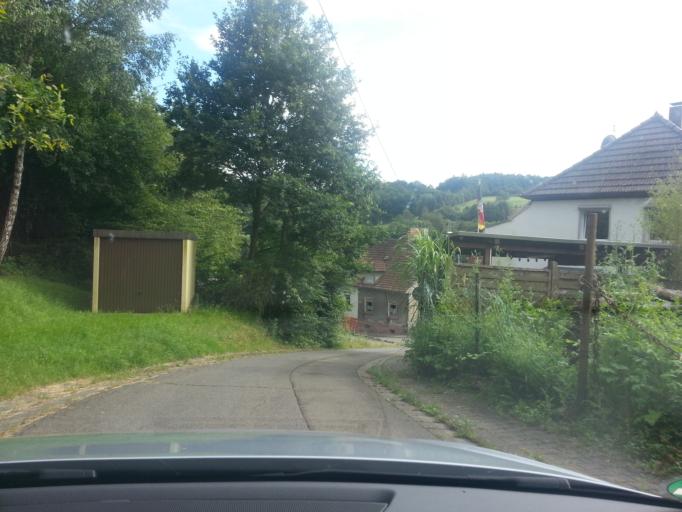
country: DE
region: Saarland
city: Schiffweiler
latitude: 49.3555
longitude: 7.1391
